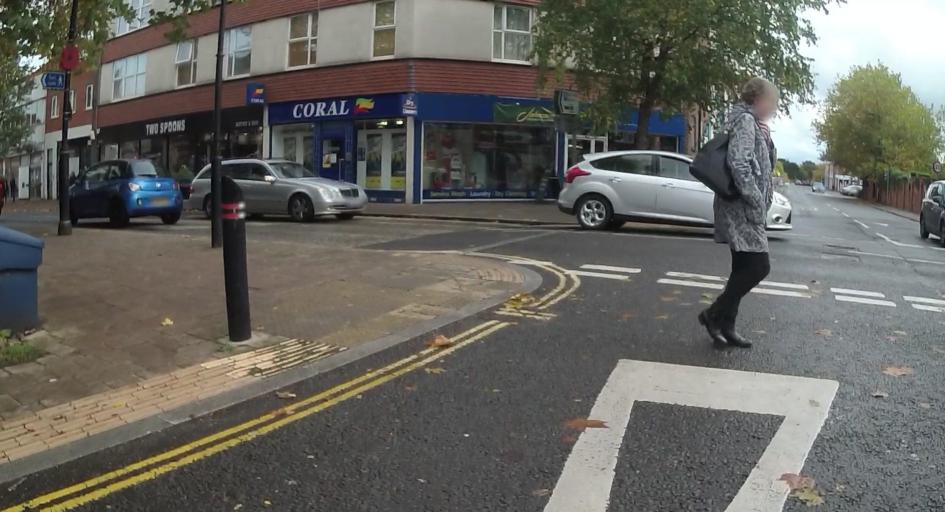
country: GB
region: England
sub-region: Hampshire
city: Fleet
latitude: 51.2804
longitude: -0.8434
